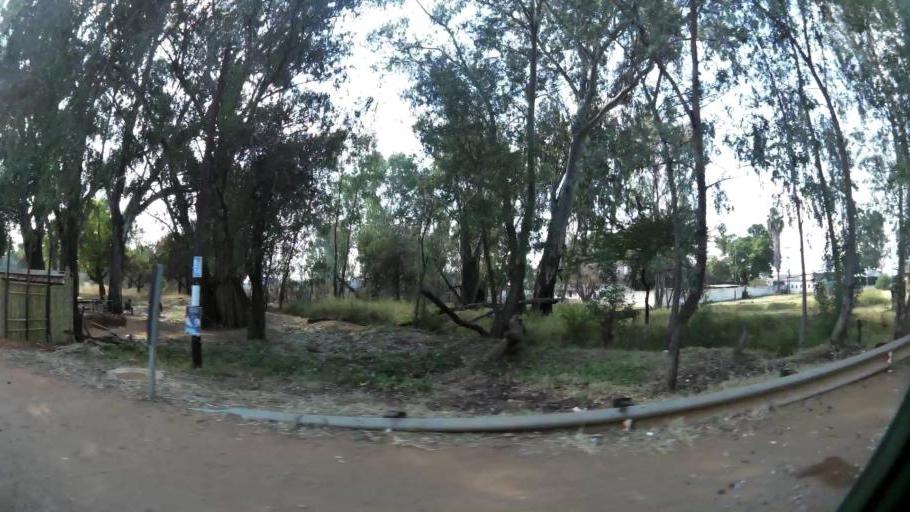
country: ZA
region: North-West
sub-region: Bojanala Platinum District Municipality
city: Rustenburg
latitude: -25.5027
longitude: 27.0940
